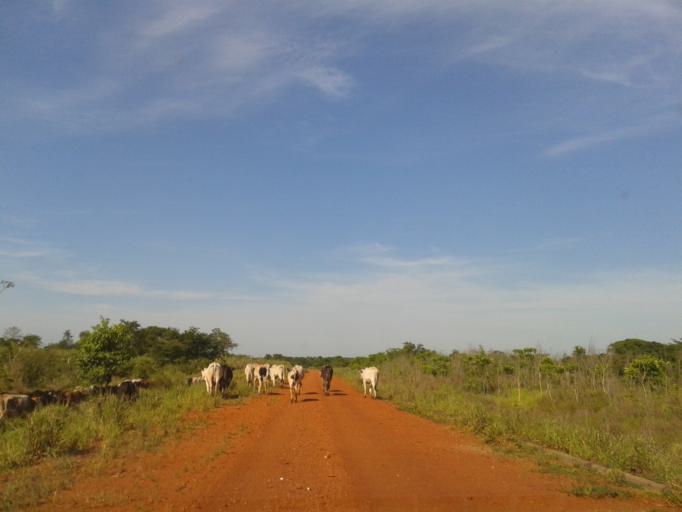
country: BR
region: Minas Gerais
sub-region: Santa Vitoria
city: Santa Vitoria
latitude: -19.1160
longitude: -50.5496
